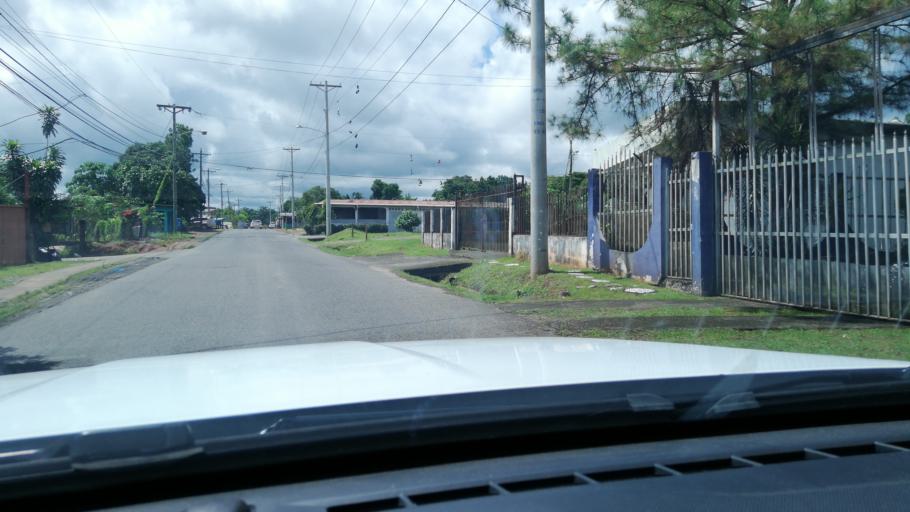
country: PA
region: Panama
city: Cabra Numero Uno
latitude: 9.1083
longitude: -79.3387
